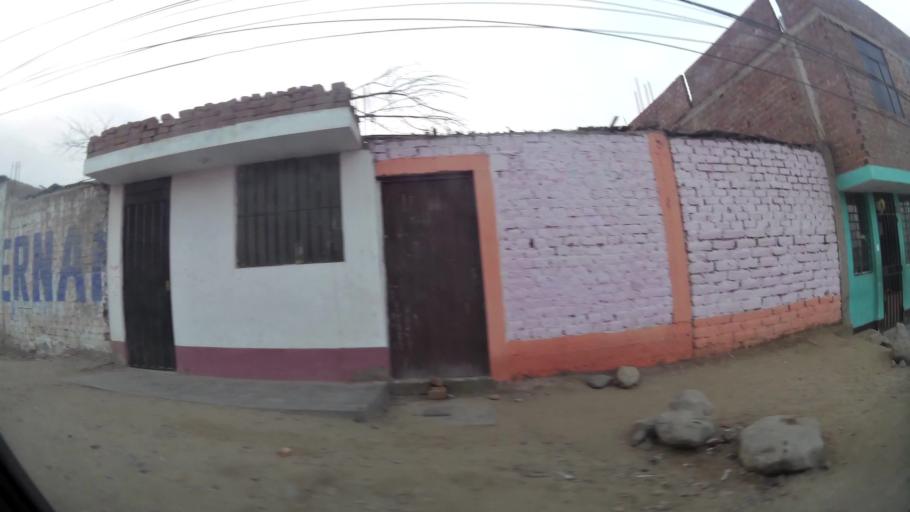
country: PE
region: La Libertad
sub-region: Provincia de Trujillo
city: El Porvenir
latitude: -8.0658
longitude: -79.0132
